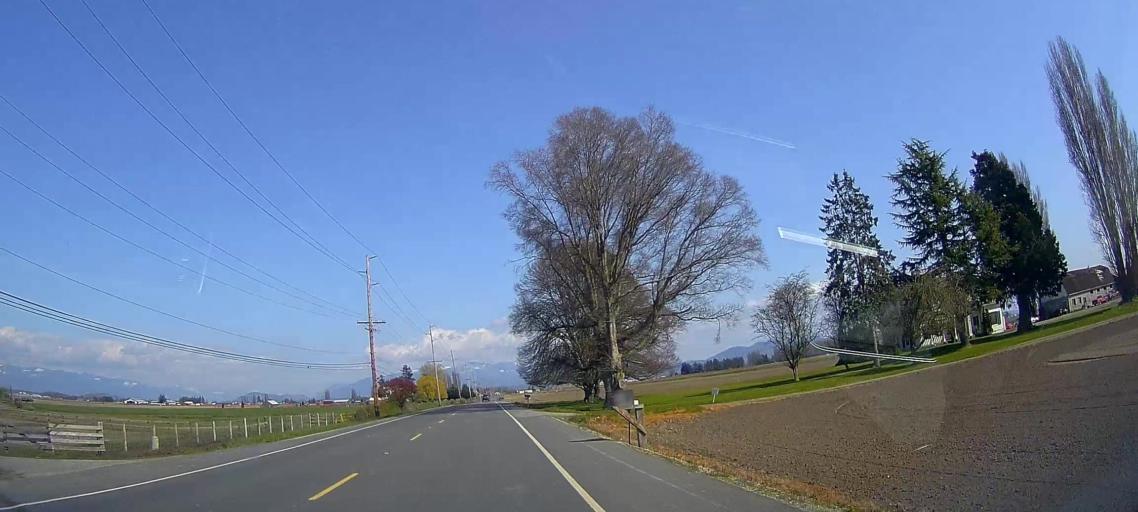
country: US
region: Washington
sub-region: Skagit County
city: Mount Vernon
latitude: 48.4209
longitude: -122.4654
